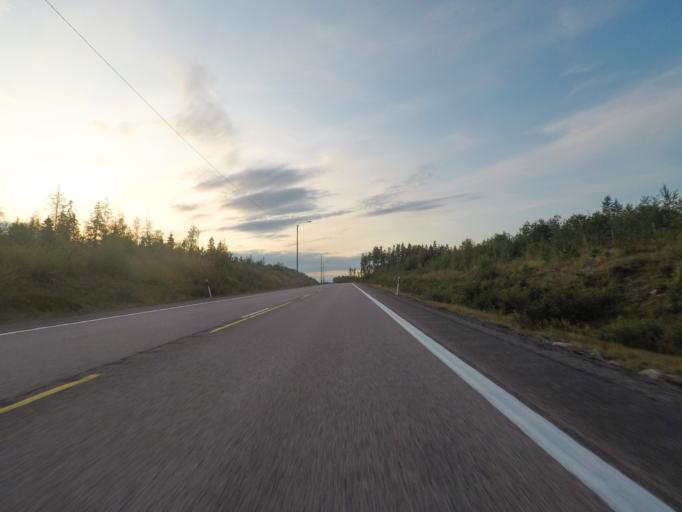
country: FI
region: Central Finland
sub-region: Jyvaeskylae
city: Toivakka
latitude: 62.1072
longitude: 25.9781
